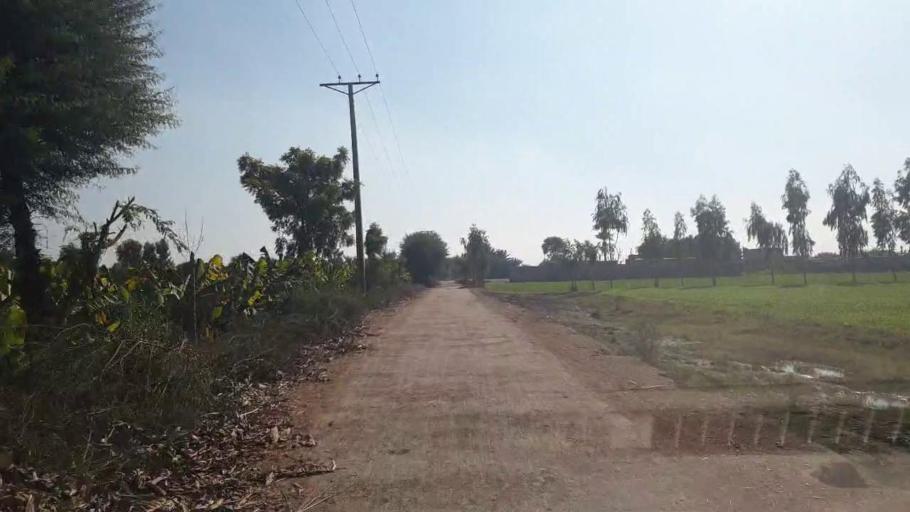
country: PK
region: Sindh
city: Shahdadpur
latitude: 25.9137
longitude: 68.5646
